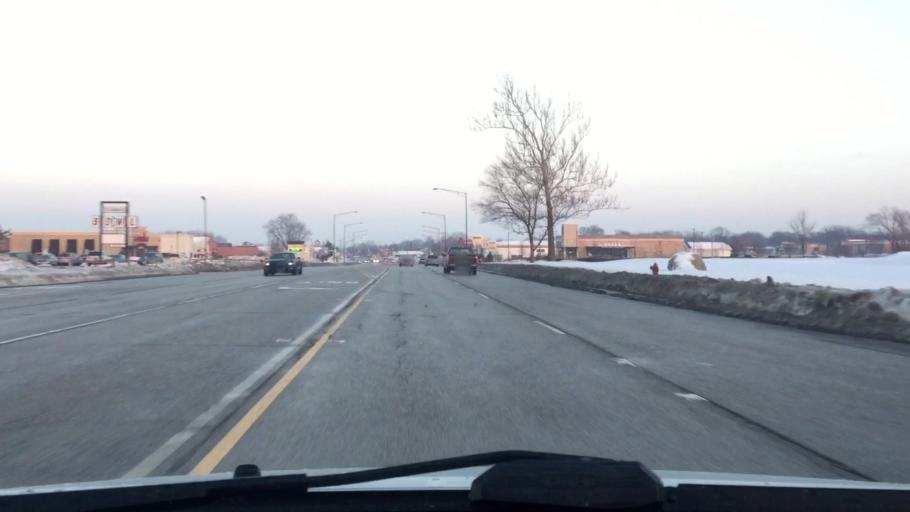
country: US
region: Illinois
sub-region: Kane County
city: Saint Charles
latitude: 41.9129
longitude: -88.3462
